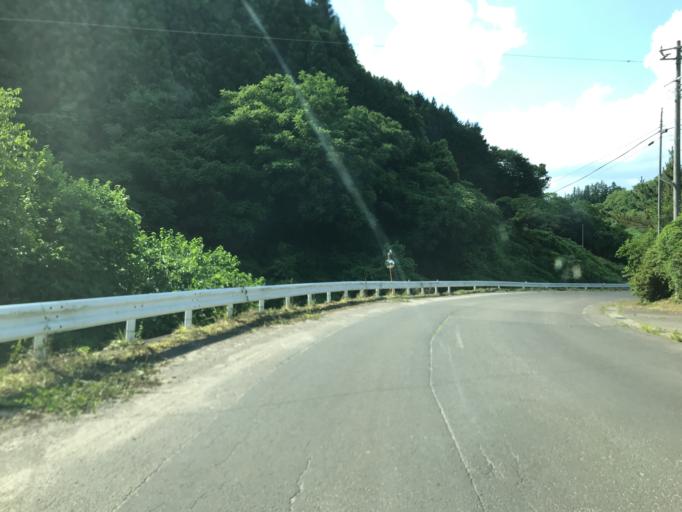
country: JP
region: Fukushima
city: Yanagawamachi-saiwaicho
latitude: 37.7875
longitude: 140.6519
